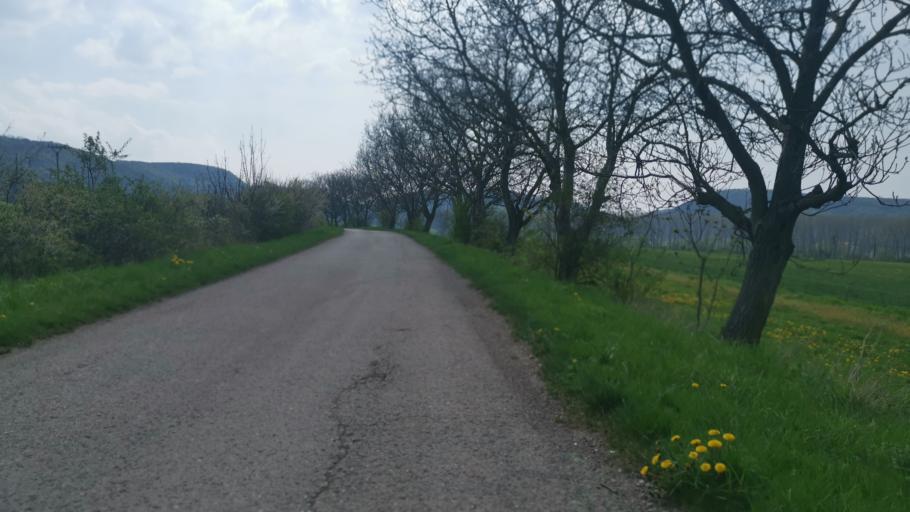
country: SK
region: Trnavsky
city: Smolenice
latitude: 48.5347
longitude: 17.3744
